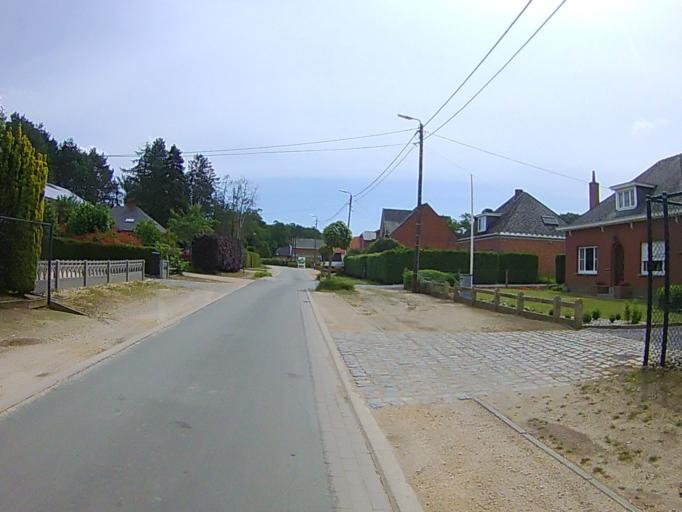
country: BE
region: Flanders
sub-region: Provincie Vlaams-Brabant
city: Keerbergen
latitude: 50.9938
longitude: 4.6421
